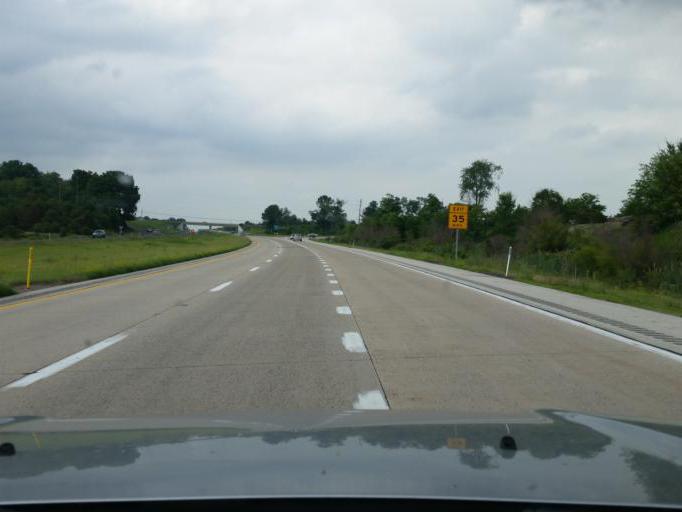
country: US
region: Pennsylvania
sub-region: Adams County
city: Lake Heritage
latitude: 39.8413
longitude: -77.1941
